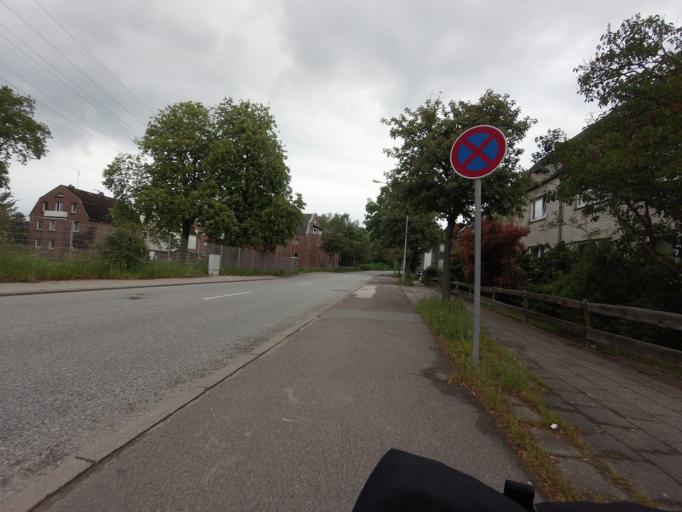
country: DE
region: Schleswig-Holstein
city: Ratekau
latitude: 53.9057
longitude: 10.7722
